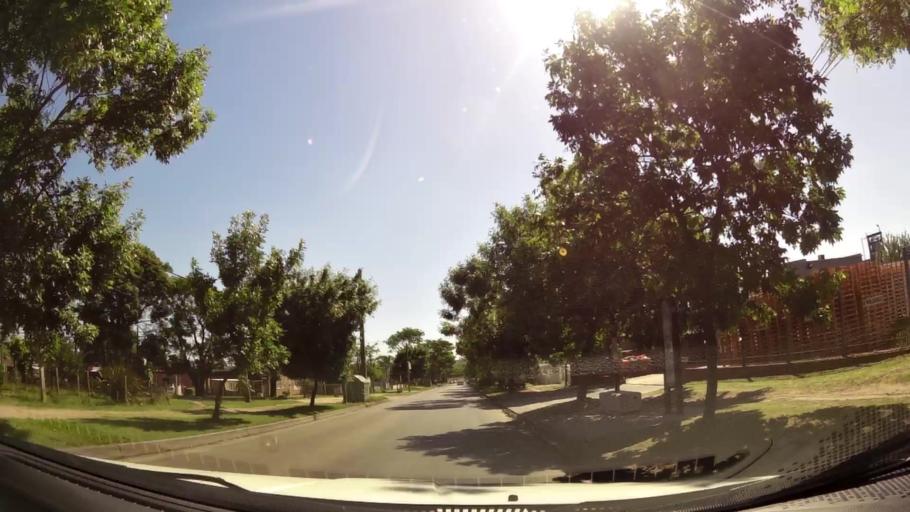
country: UY
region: Montevideo
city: Pajas Blancas
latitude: -34.8374
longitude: -56.2610
